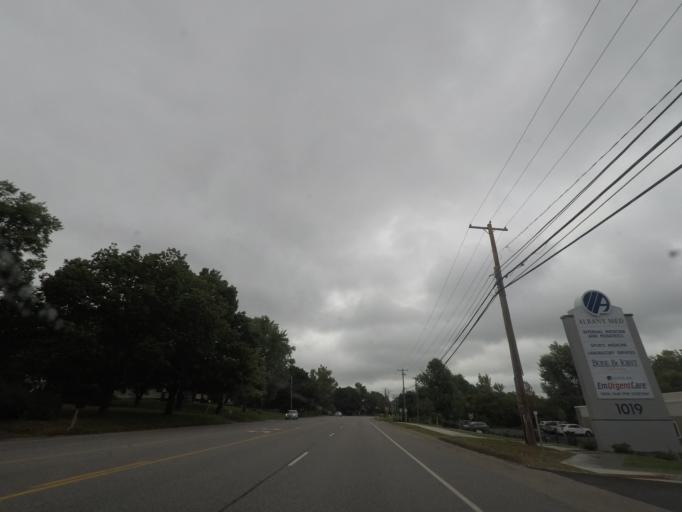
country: US
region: New York
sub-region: Albany County
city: Cohoes
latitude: 42.7740
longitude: -73.7522
